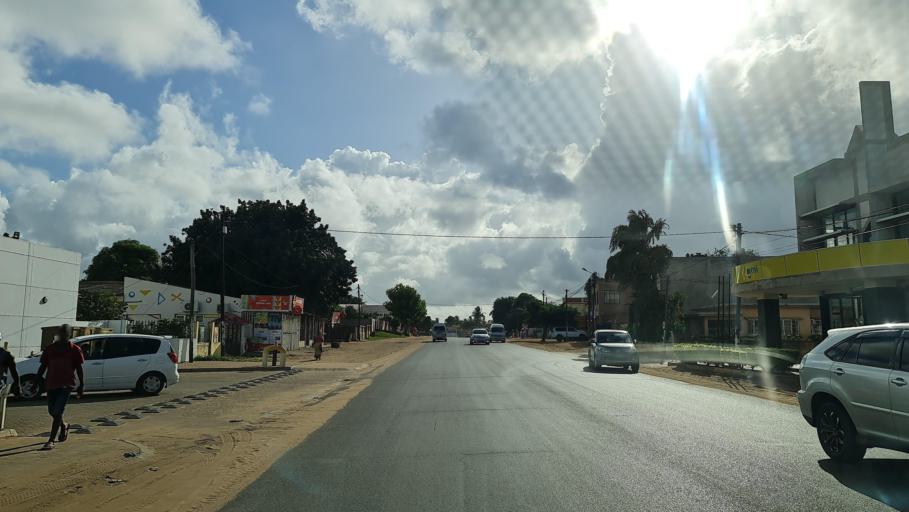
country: MZ
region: Gaza
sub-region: Xai-Xai District
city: Xai-Xai
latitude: -25.0563
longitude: 33.6654
